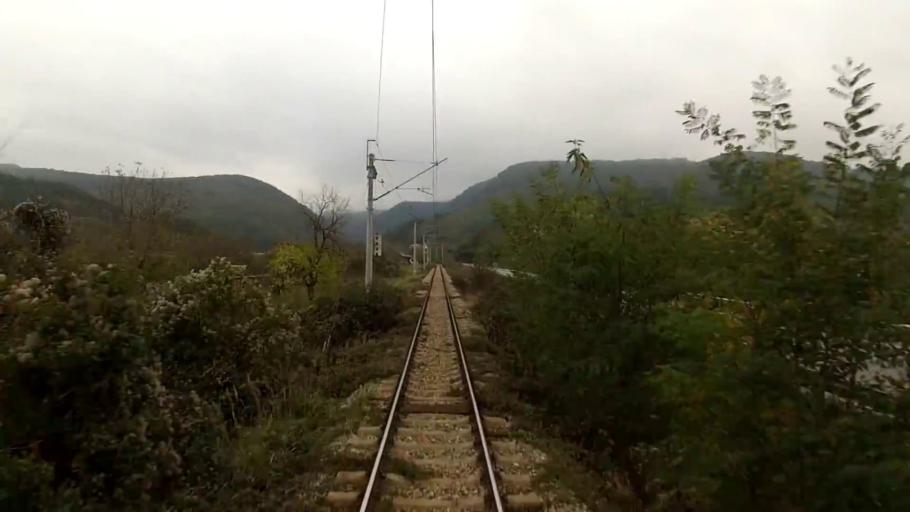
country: RS
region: Central Serbia
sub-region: Pirotski Okrug
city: Dimitrovgrad
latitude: 42.9803
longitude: 22.8500
